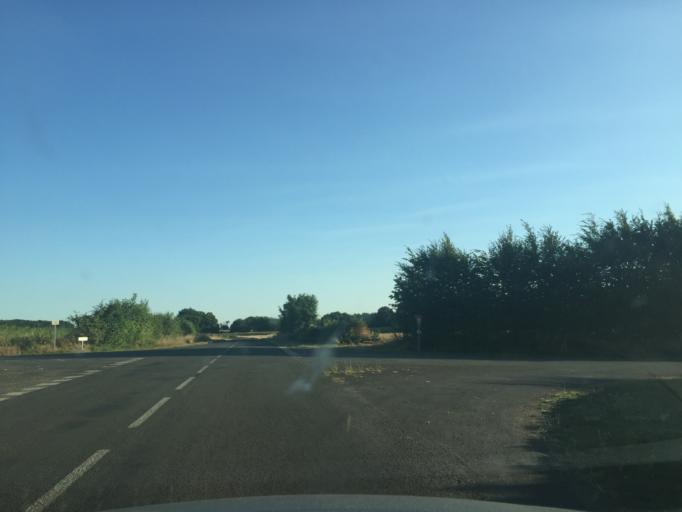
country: FR
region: Poitou-Charentes
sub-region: Departement des Deux-Sevres
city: Lezay
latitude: 46.1987
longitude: -0.0379
